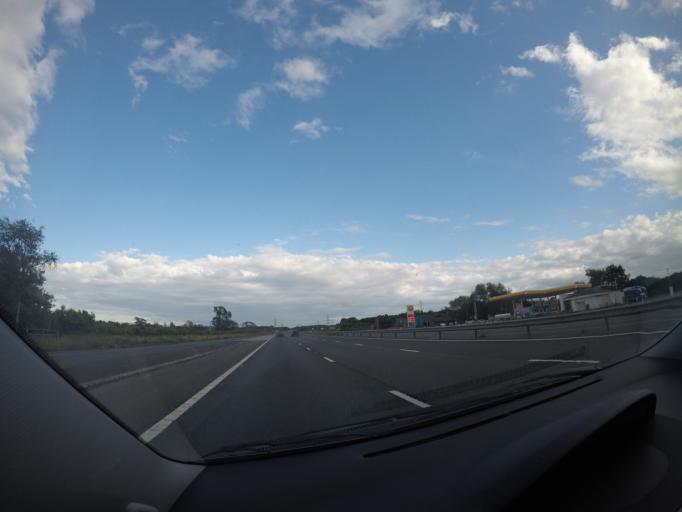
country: GB
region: England
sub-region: Cumbria
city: Carlisle
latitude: 54.9515
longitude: -2.9793
